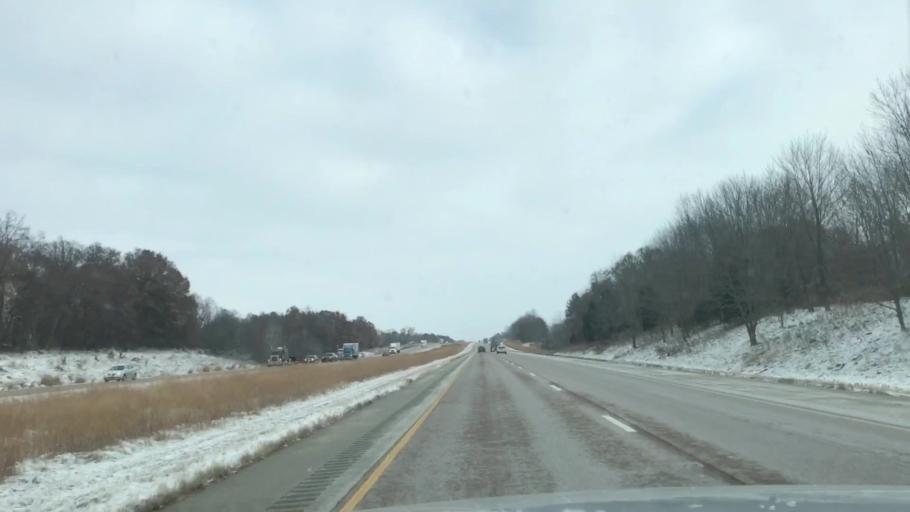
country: US
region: Illinois
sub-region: Macoupin County
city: Mount Olive
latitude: 39.1006
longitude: -89.7341
